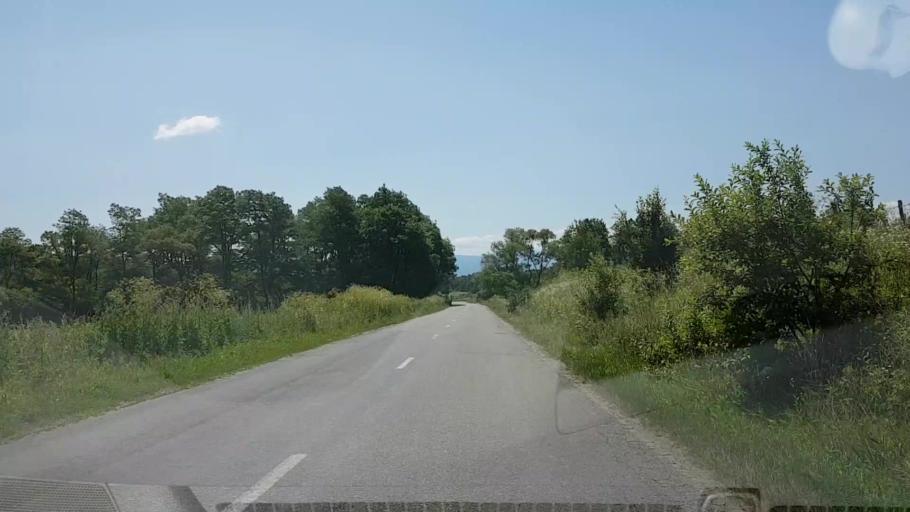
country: RO
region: Brasov
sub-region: Comuna Cincu
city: Cincu
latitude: 45.8803
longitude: 24.8144
